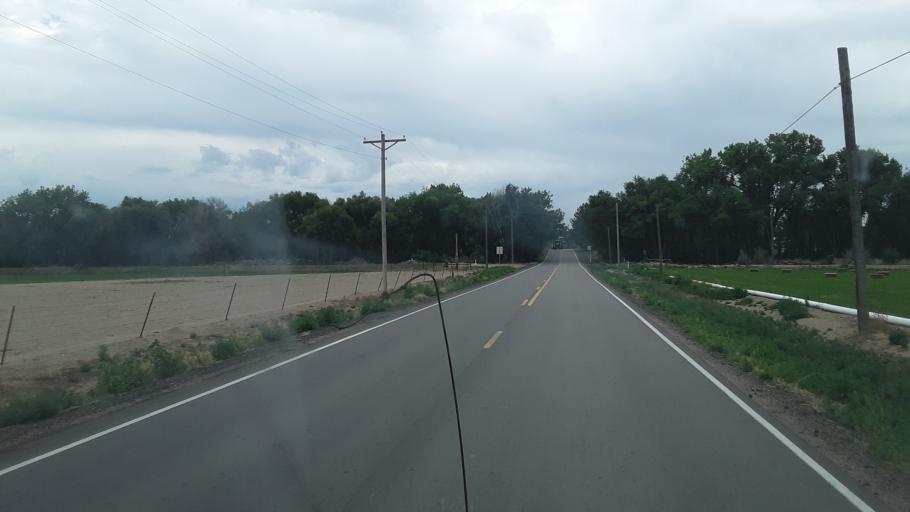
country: US
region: Colorado
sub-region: Otero County
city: Fowler
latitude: 38.1360
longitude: -104.0226
